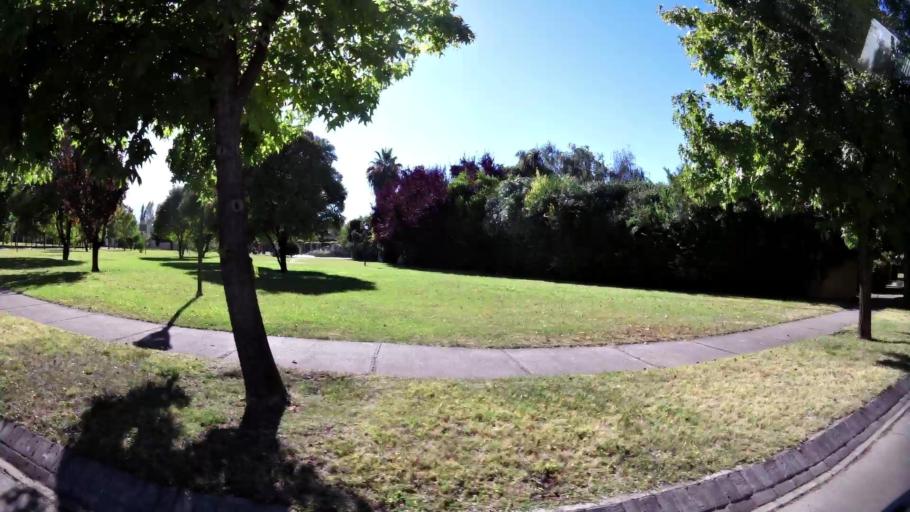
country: CL
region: O'Higgins
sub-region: Provincia de Cachapoal
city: Rancagua
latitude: -34.1906
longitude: -70.7165
